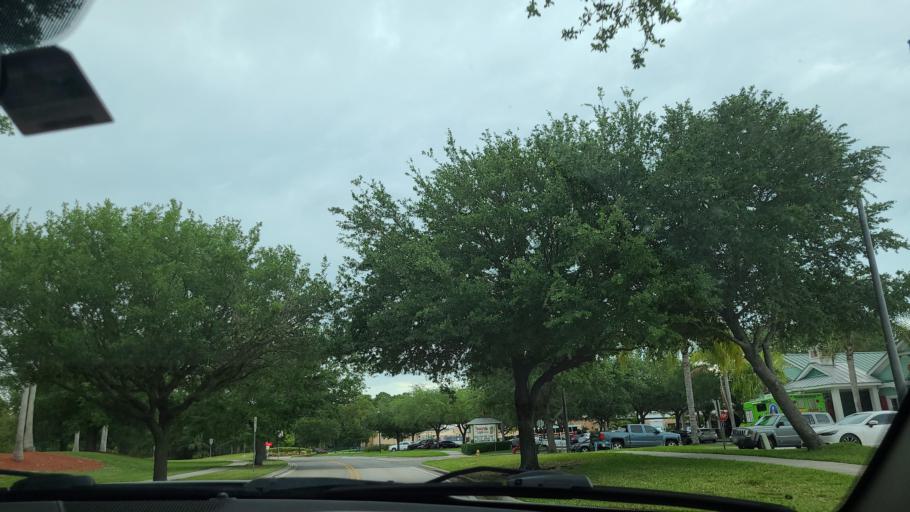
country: US
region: Florida
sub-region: Brevard County
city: Grant-Valkaria
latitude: 27.9524
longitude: -80.6590
